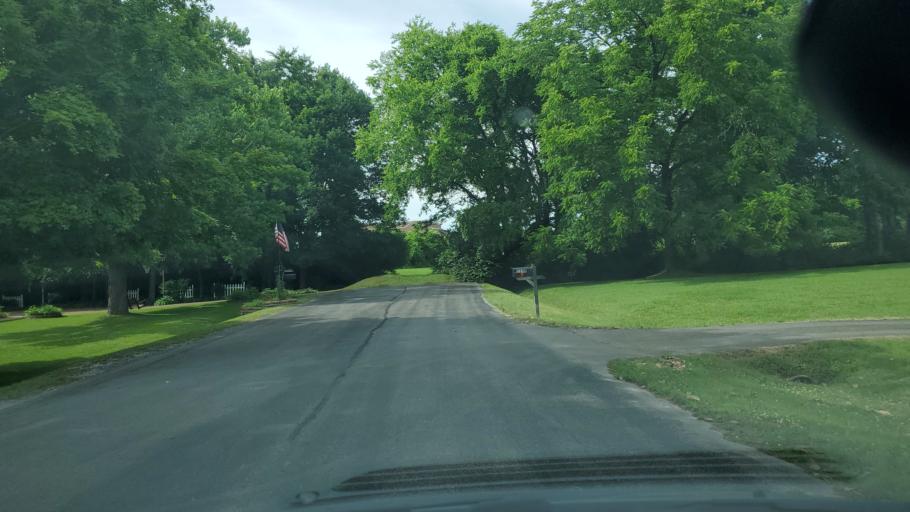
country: US
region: Tennessee
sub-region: Davidson County
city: Lakewood
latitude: 36.2090
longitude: -86.6895
